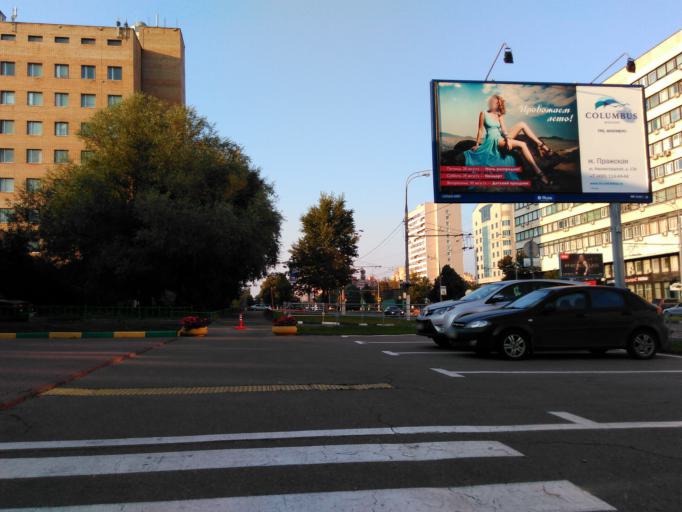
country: RU
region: Moskovskaya
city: Cheremushki
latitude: 55.6627
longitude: 37.5461
